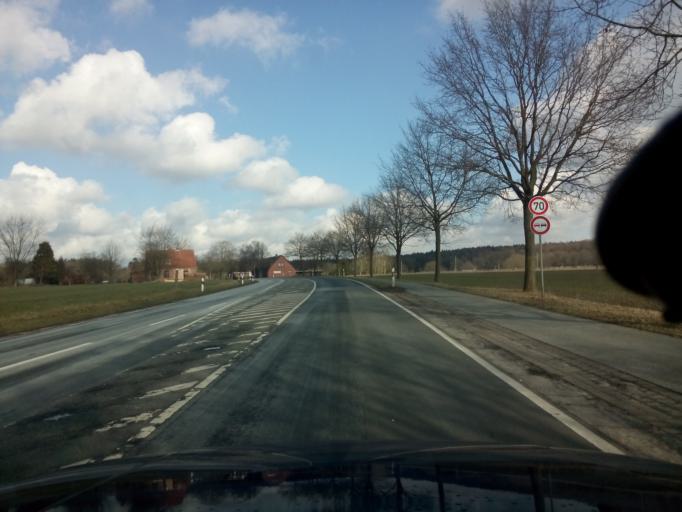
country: DE
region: Lower Saxony
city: Gnarrenburg
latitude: 53.3895
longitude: 8.9687
